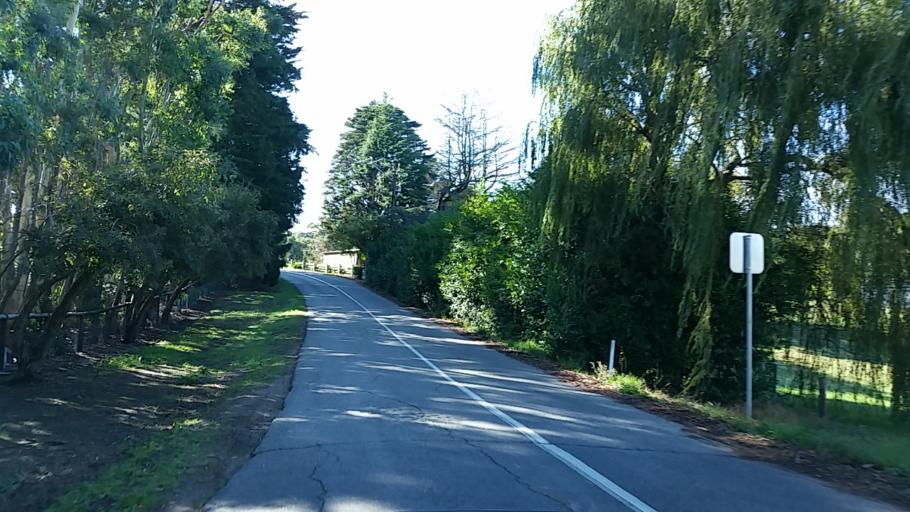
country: AU
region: South Australia
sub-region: Adelaide Hills
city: Adelaide Hills
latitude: -34.9446
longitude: 138.7260
